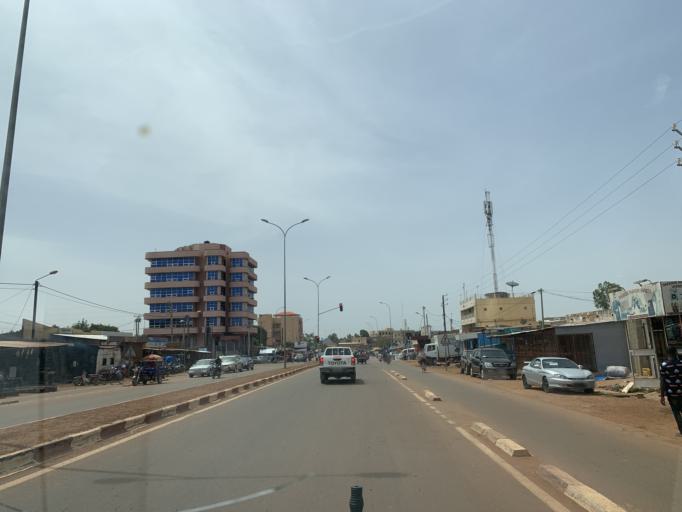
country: BF
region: Centre
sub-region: Kadiogo Province
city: Ouagadougou
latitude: 12.3384
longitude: -1.5100
